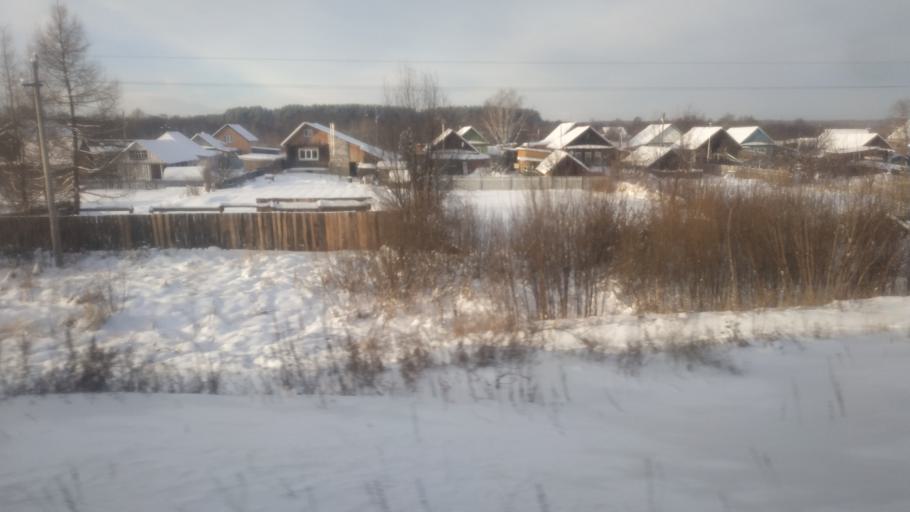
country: RU
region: Udmurtiya
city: Kizner
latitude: 56.2767
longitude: 51.4985
